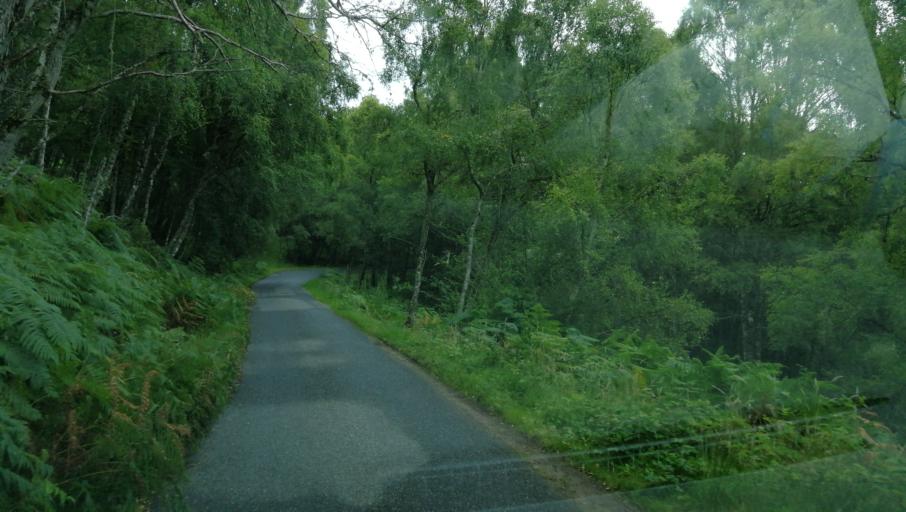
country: GB
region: Scotland
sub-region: Highland
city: Beauly
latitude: 57.3199
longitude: -4.8059
